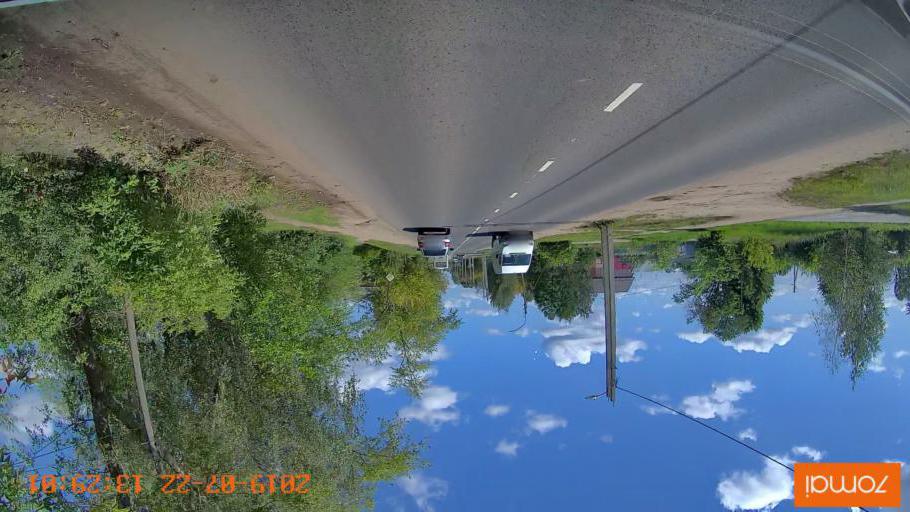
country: RU
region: Ivanovo
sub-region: Gorod Ivanovo
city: Ivanovo
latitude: 57.0450
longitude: 40.9437
